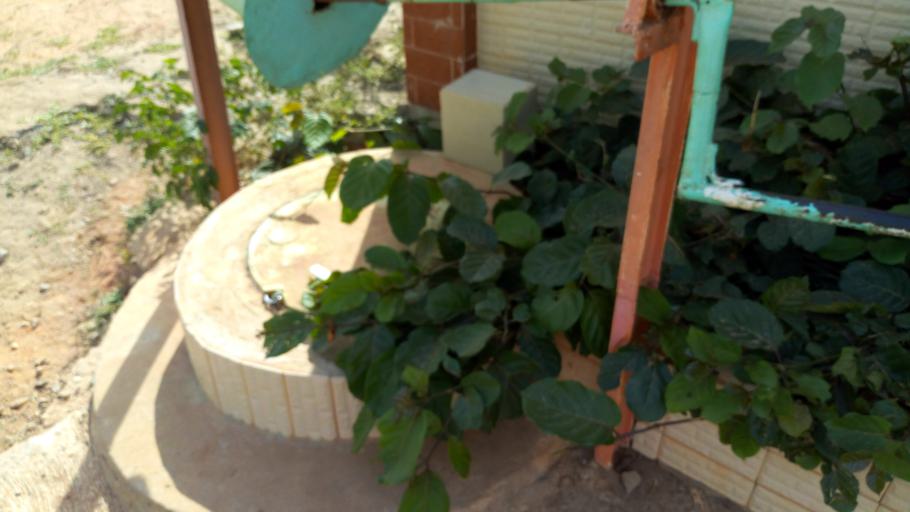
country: CI
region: Vallee du Bandama
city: Bouake
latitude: 7.7091
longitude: -5.0435
